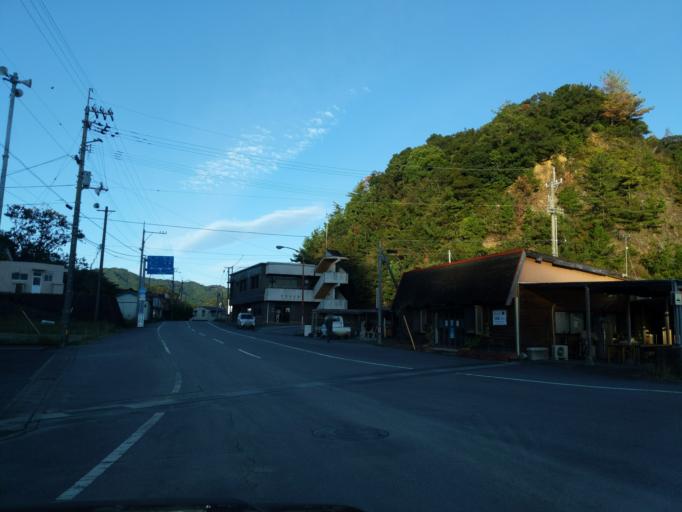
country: JP
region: Kochi
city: Muroto-misakicho
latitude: 33.5433
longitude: 134.2996
